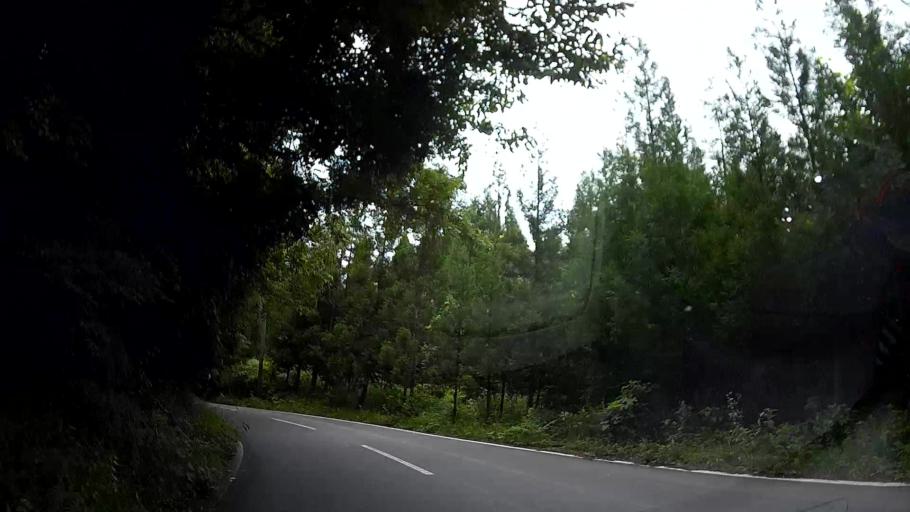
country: JP
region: Oita
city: Hita
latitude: 33.1397
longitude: 130.9746
